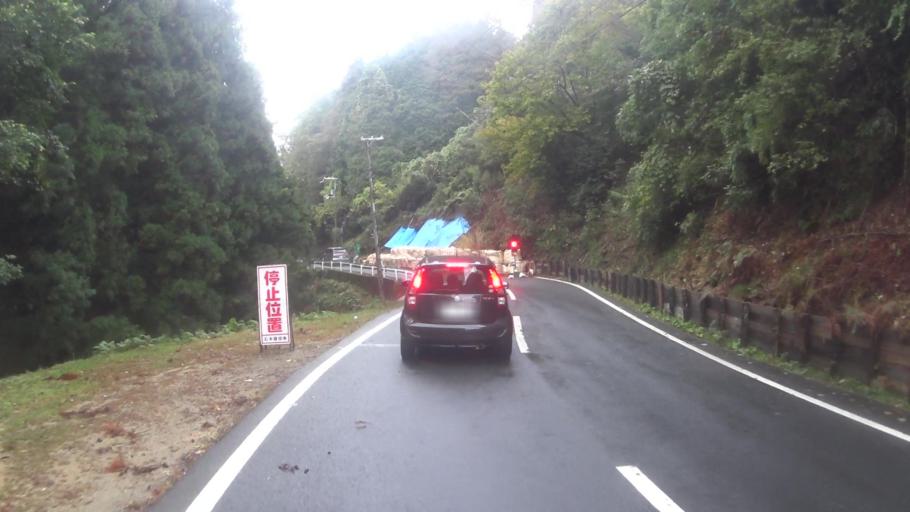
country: JP
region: Kyoto
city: Miyazu
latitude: 35.5267
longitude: 135.0515
